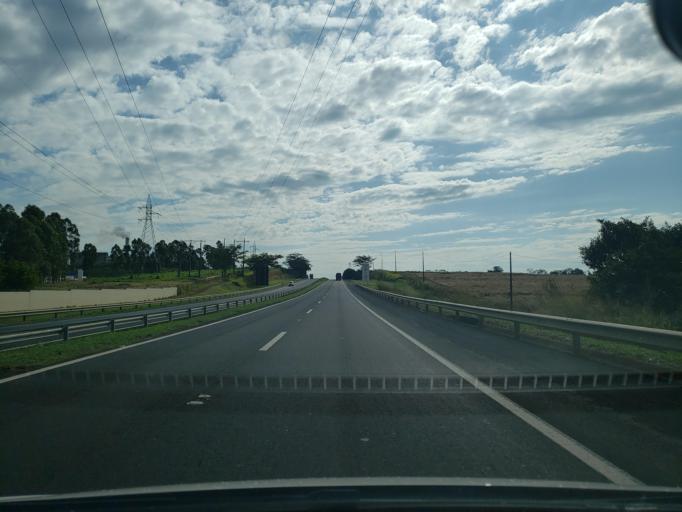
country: BR
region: Sao Paulo
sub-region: Lins
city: Lins
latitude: -21.6775
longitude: -49.7730
